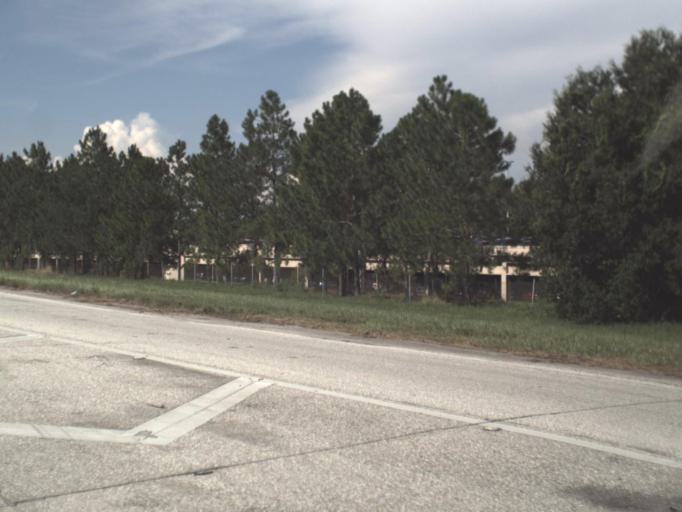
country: US
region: Florida
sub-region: Hillsborough County
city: Mango
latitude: 27.9776
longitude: -82.3266
